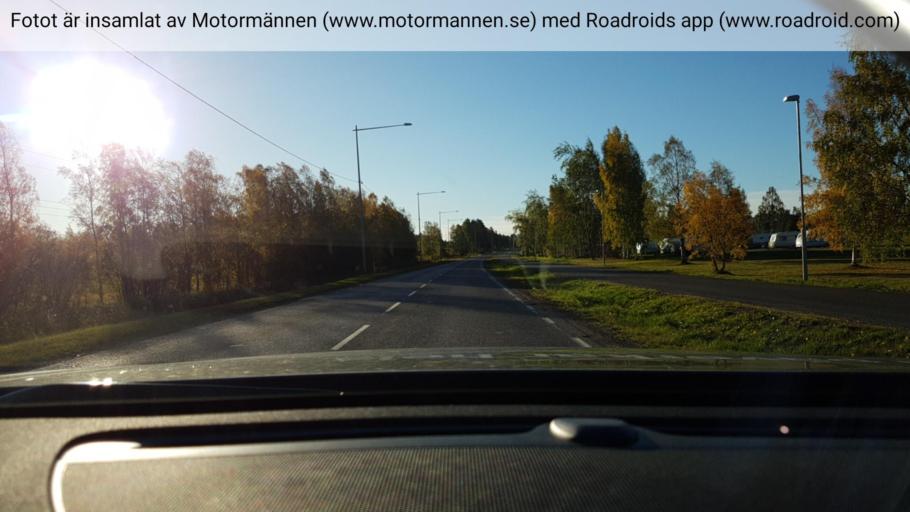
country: SE
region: Norrbotten
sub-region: Lulea Kommun
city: Gammelstad
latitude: 65.6378
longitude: 22.0259
